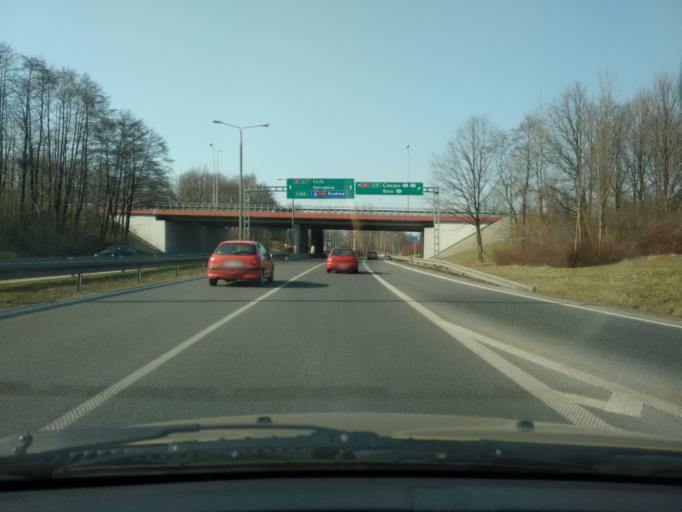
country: PL
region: Silesian Voivodeship
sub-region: Bielsko-Biala
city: Bielsko-Biala
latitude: 49.8480
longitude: 19.0306
